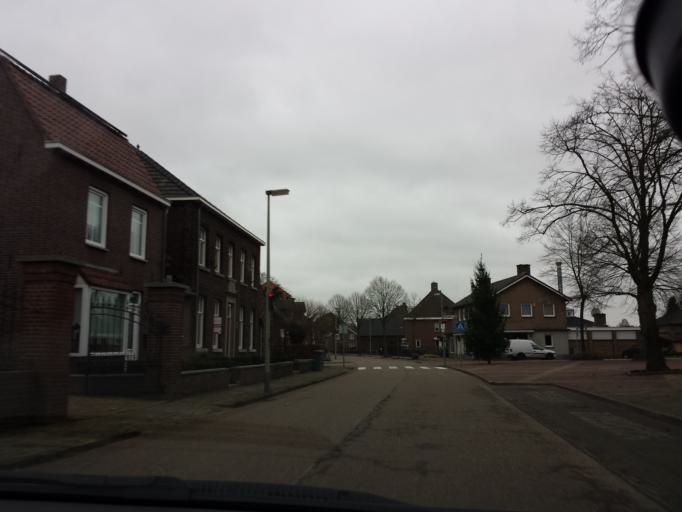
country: NL
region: Limburg
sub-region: Gemeente Roerdalen
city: Posterholt
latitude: 51.1230
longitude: 6.0320
